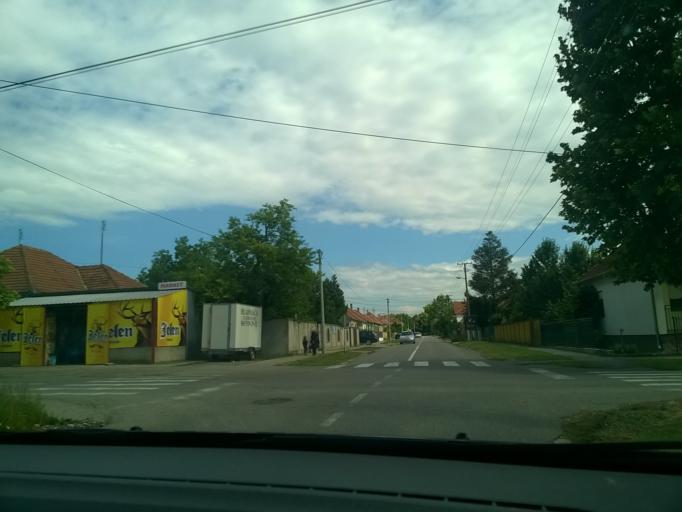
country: RS
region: Autonomna Pokrajina Vojvodina
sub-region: Sremski Okrug
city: Ruma
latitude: 45.0166
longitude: 19.8167
